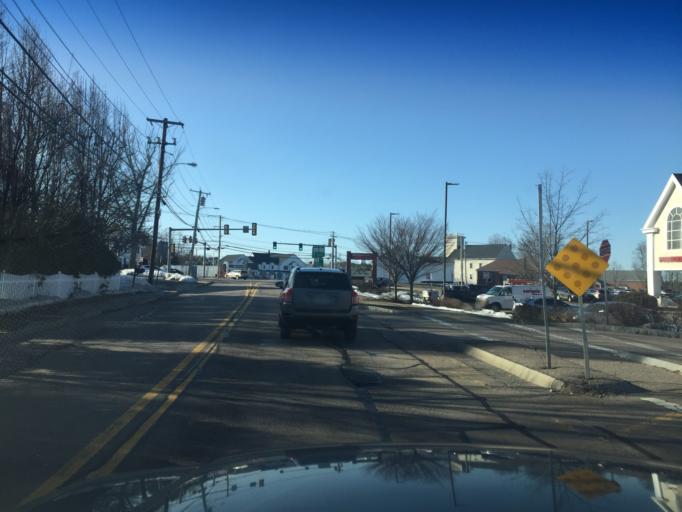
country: US
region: Massachusetts
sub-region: Norfolk County
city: Bellingham
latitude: 42.0859
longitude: -71.4730
